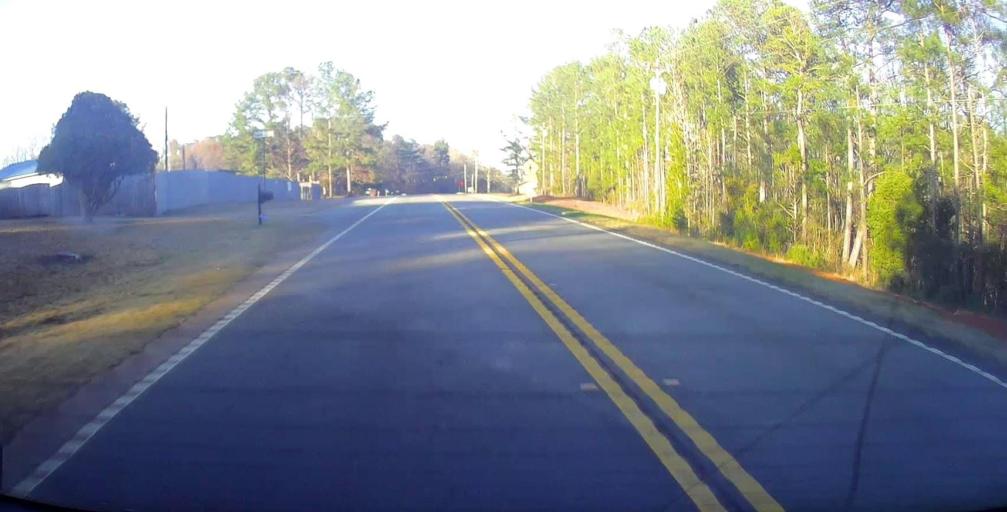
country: US
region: Georgia
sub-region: Upson County
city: Thomaston
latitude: 32.8580
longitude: -84.4165
